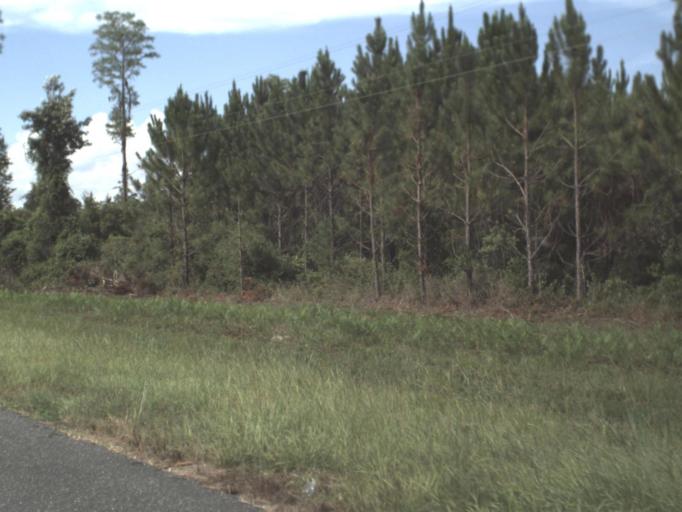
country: US
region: Florida
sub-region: Taylor County
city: Perry
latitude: 30.2310
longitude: -83.6173
